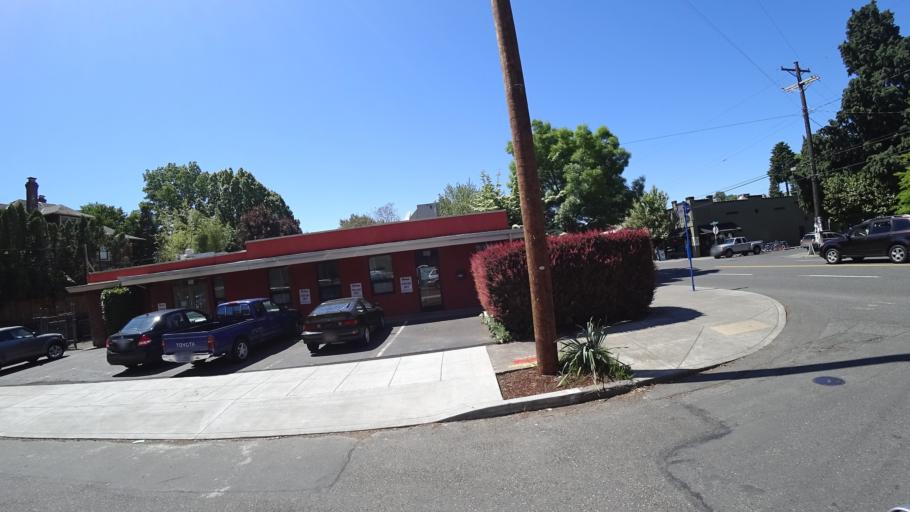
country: US
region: Oregon
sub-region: Multnomah County
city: Portland
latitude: 45.5119
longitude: -122.6422
